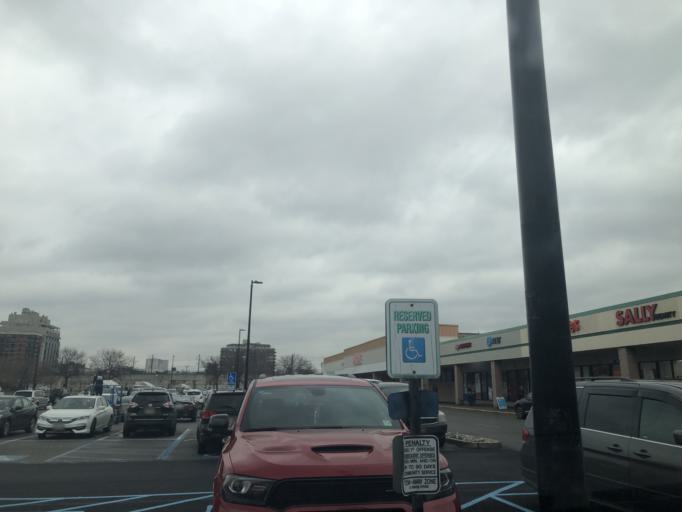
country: US
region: New Jersey
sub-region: Hudson County
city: Hoboken
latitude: 40.7322
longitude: -74.0381
